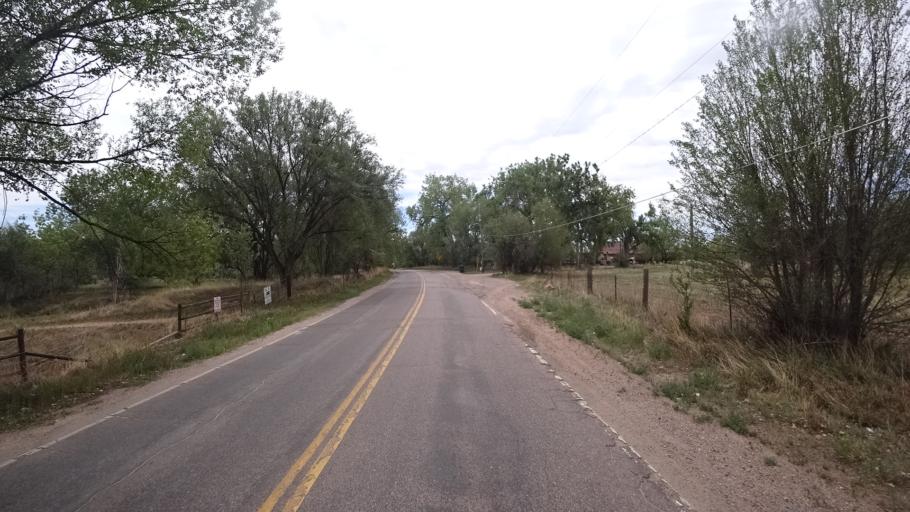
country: US
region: Colorado
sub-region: El Paso County
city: Fountain
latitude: 38.6767
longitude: -104.7010
